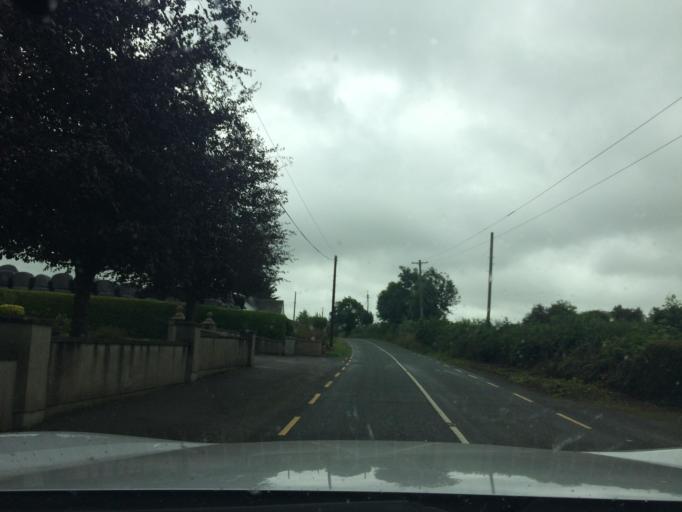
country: IE
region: Munster
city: Cashel
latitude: 52.5415
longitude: -7.8929
